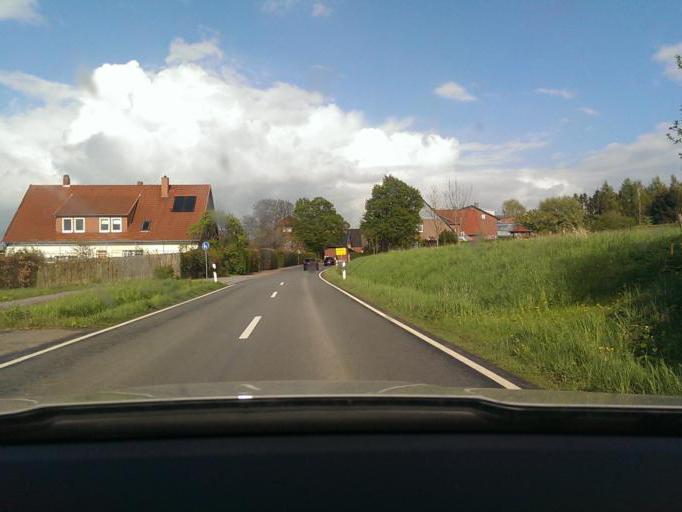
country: DE
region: Lower Saxony
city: Rehren
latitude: 52.2354
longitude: 9.2747
